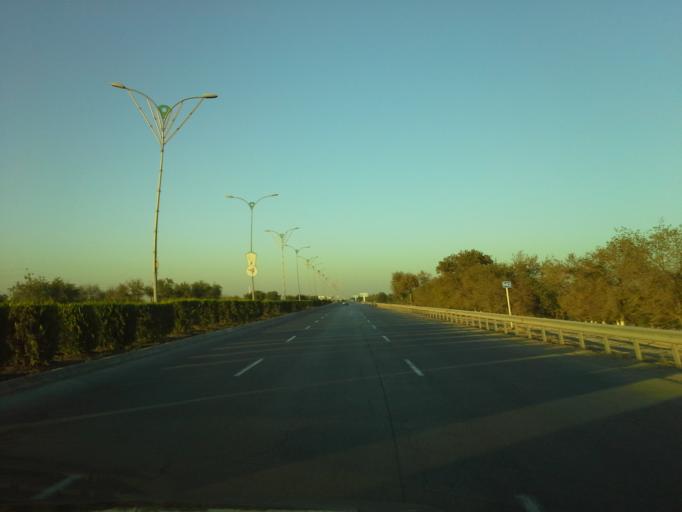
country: TM
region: Dasoguz
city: Dasoguz
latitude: 41.7946
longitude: 59.8888
